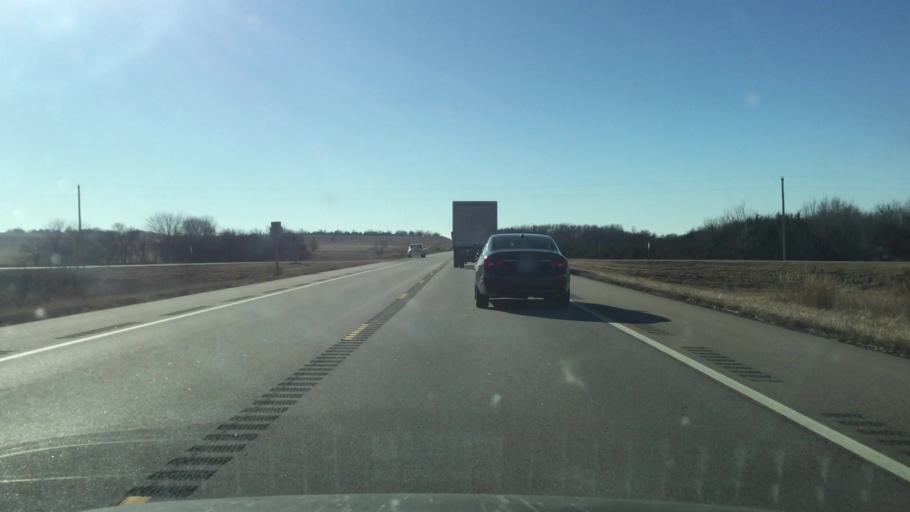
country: US
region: Kansas
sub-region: Allen County
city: Iola
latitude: 38.0251
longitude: -95.3809
